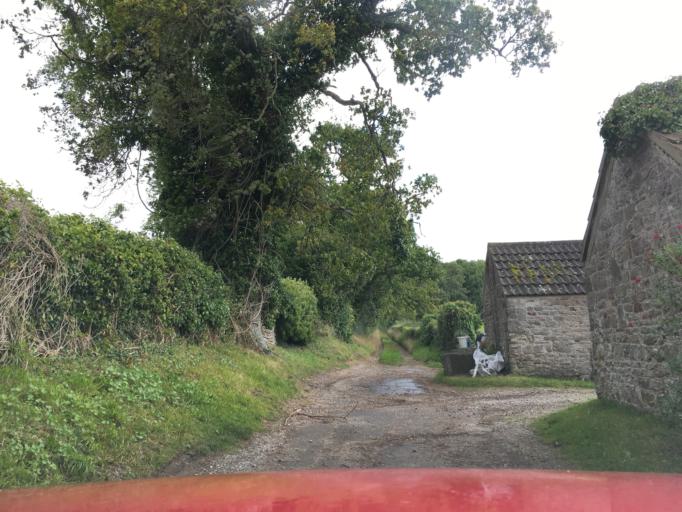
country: GB
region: England
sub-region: South Gloucestershire
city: Falfield
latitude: 51.6251
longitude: -2.4526
